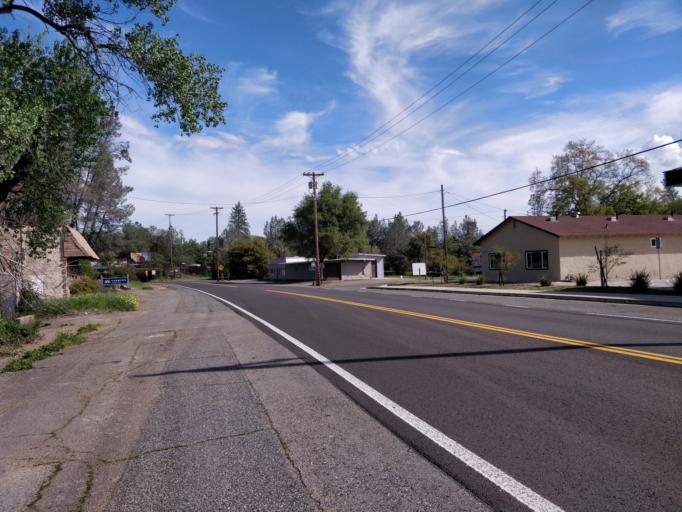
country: US
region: California
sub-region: Shasta County
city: Central Valley (historical)
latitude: 40.6830
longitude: -122.3772
